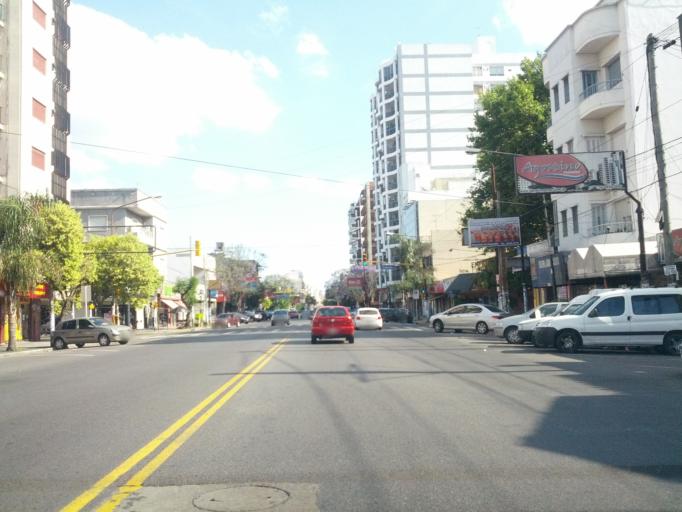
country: AR
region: Buenos Aires
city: San Justo
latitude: -34.6467
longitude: -58.5644
